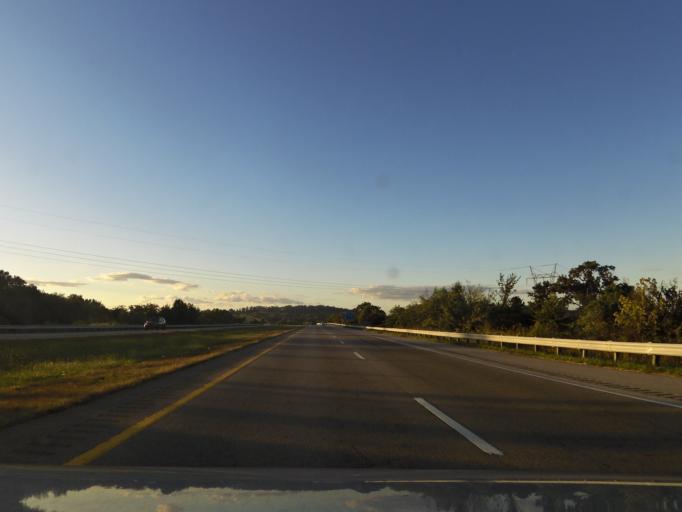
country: US
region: Tennessee
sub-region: Blount County
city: Eagleton Village
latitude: 35.8210
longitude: -83.9529
